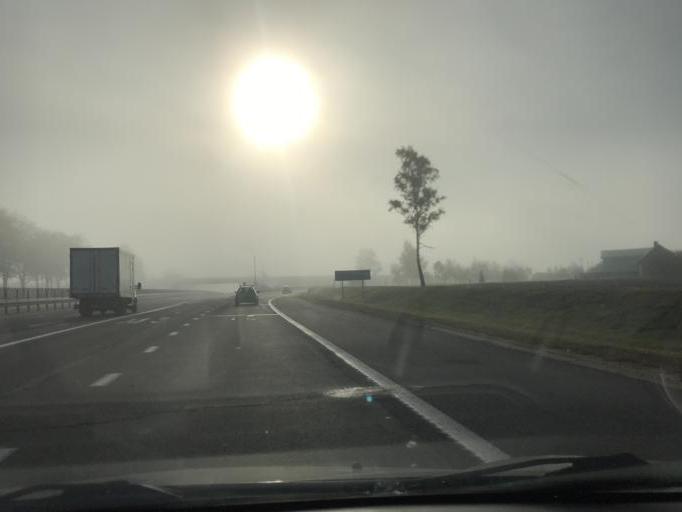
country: BY
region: Minsk
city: Pryvol'ny
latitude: 53.7939
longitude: 27.8159
